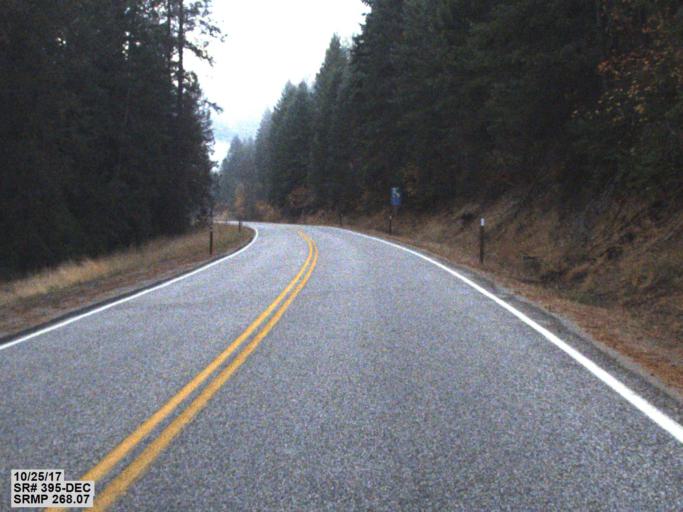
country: CA
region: British Columbia
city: Grand Forks
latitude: 48.9687
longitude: -118.2221
